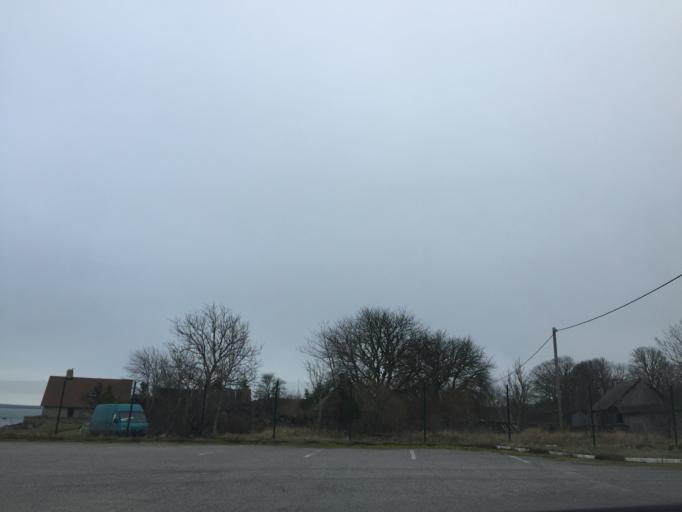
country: EE
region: Saare
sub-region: Kuressaare linn
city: Kuressaare
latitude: 58.5448
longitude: 22.2175
